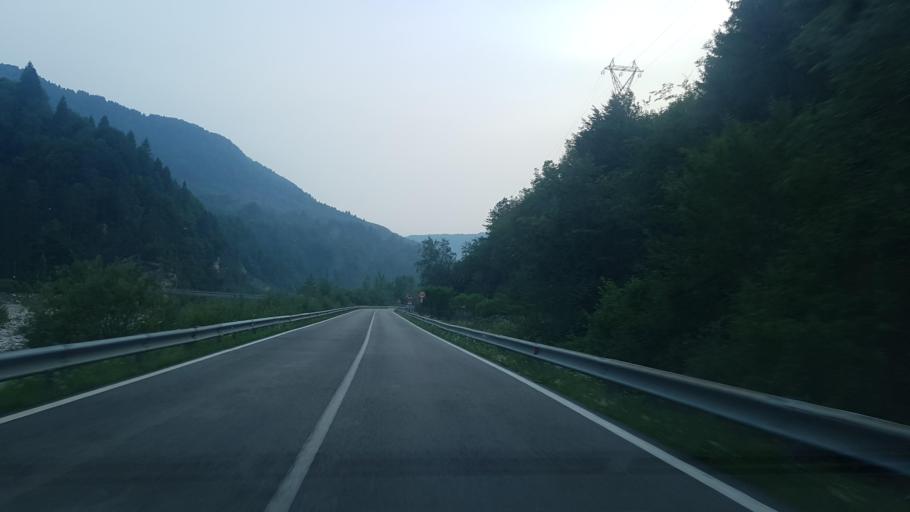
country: IT
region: Friuli Venezia Giulia
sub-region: Provincia di Udine
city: Zuglio
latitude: 46.4707
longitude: 13.0671
